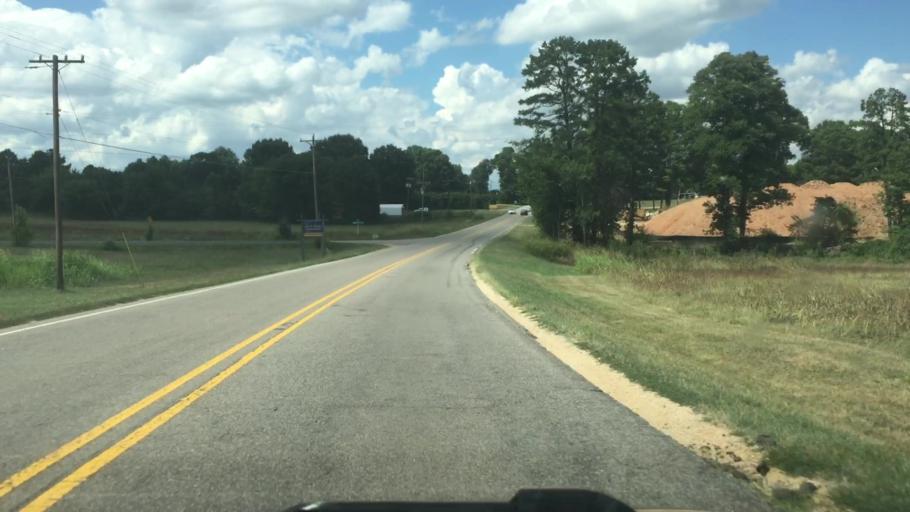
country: US
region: North Carolina
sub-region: Gaston County
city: Davidson
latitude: 35.4980
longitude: -80.7699
